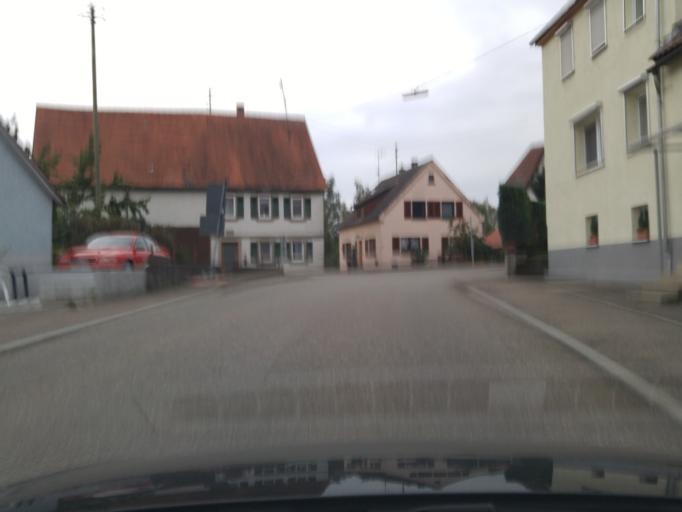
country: DE
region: Baden-Wuerttemberg
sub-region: Regierungsbezirk Stuttgart
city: Bretzfeld
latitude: 49.1733
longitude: 9.4254
